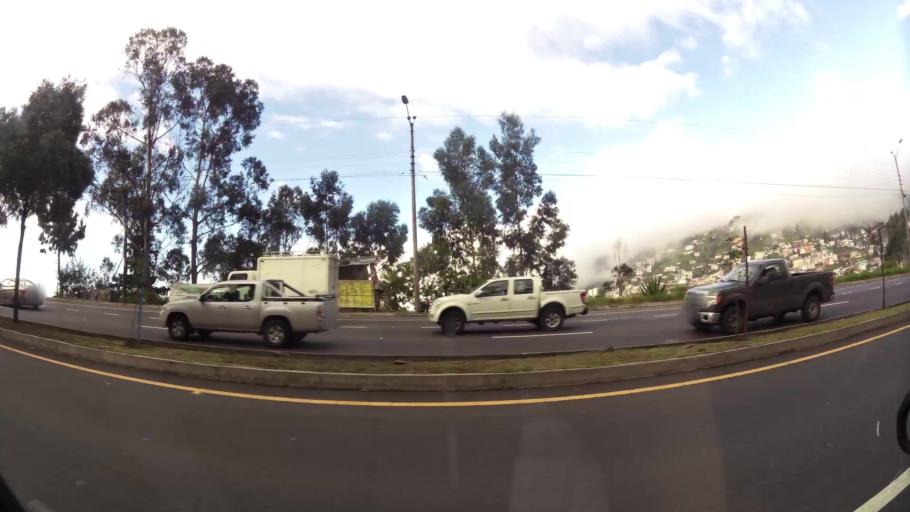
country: EC
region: Pichincha
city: Quito
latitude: -0.2334
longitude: -78.4885
